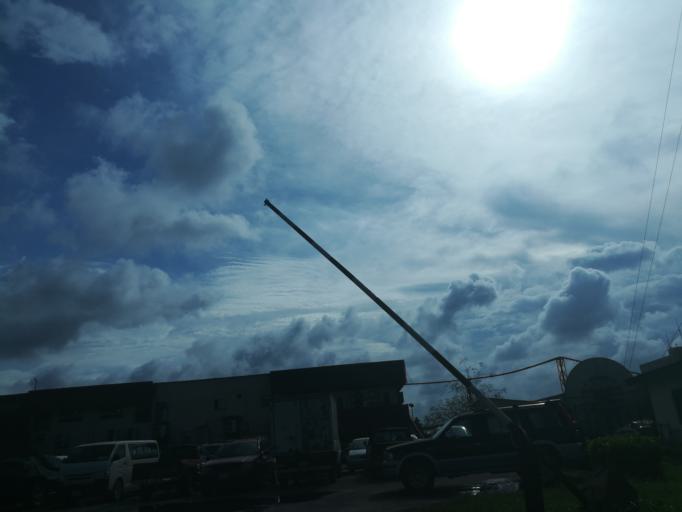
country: NG
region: Lagos
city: Ikeja
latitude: 6.6165
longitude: 3.3551
